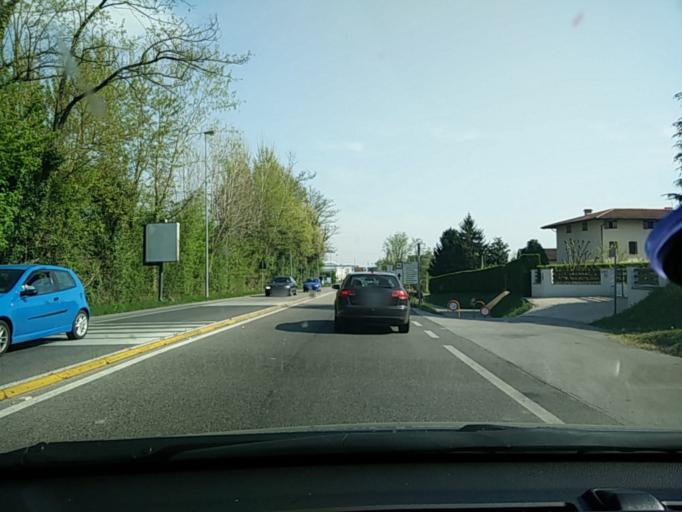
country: IT
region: Friuli Venezia Giulia
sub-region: Provincia di Pordenone
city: Pordenone
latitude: 45.9434
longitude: 12.6531
